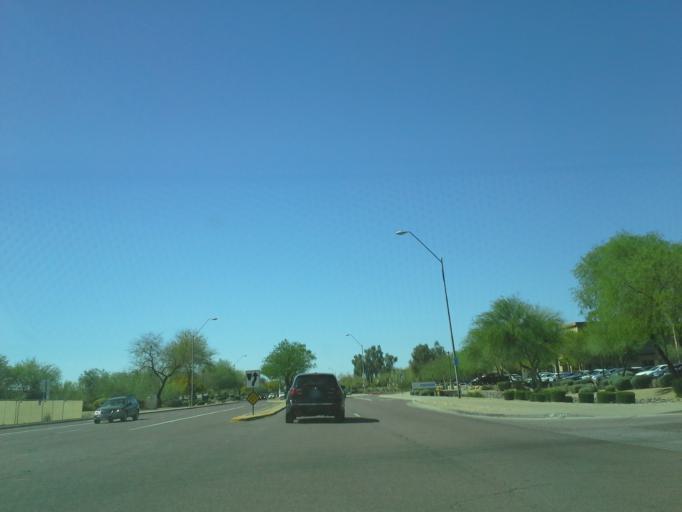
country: US
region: Arizona
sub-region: Maricopa County
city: Paradise Valley
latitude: 33.6257
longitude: -111.8992
